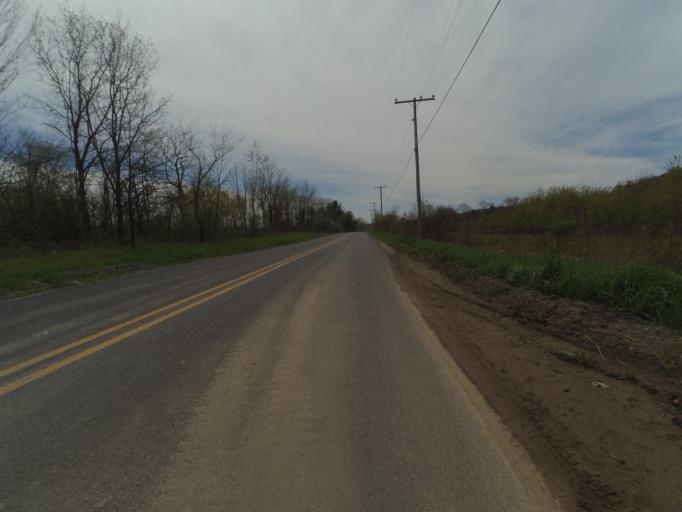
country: US
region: Pennsylvania
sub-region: Blair County
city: Tyrone
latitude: 40.6982
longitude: -78.1732
